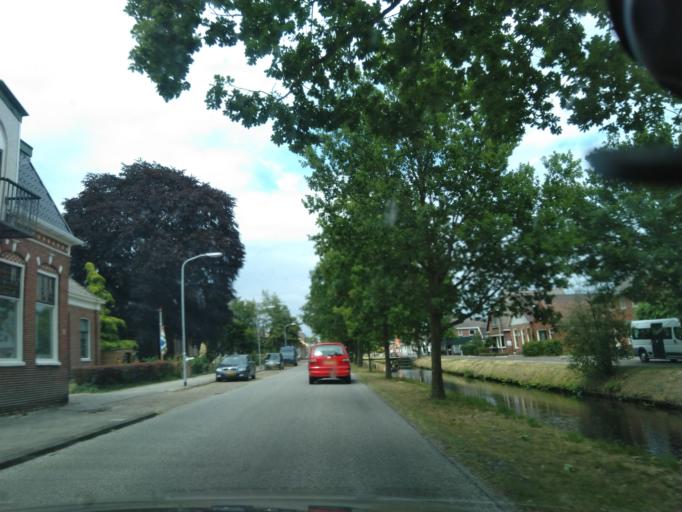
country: NL
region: Groningen
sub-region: Gemeente Pekela
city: Oude Pekela
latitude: 53.0867
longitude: 6.9798
